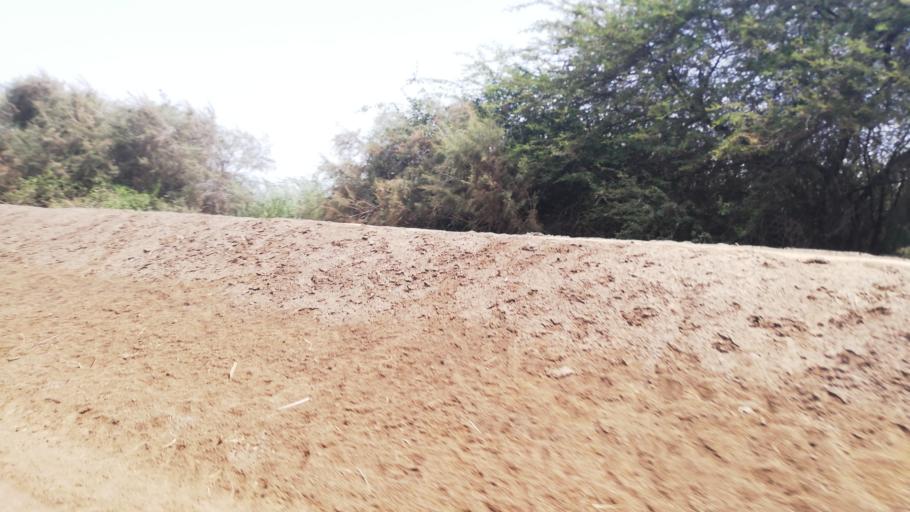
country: SN
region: Saint-Louis
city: Saint-Louis
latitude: 16.4054
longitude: -16.2962
